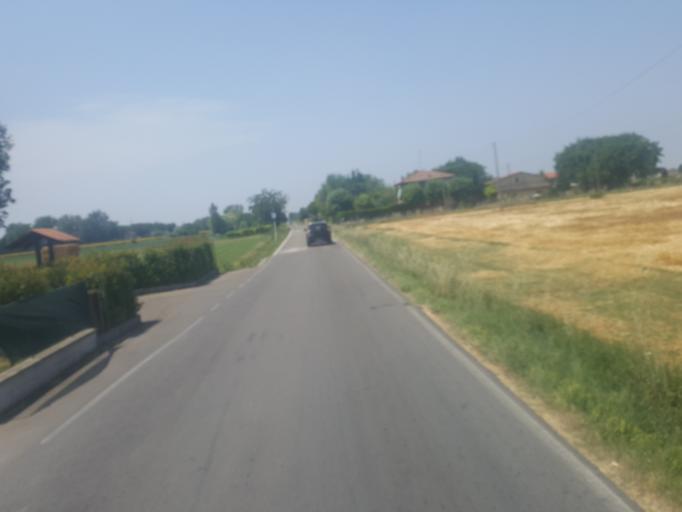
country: IT
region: Emilia-Romagna
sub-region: Provincia di Modena
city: Castelfranco Emilia
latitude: 44.6208
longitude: 11.0522
